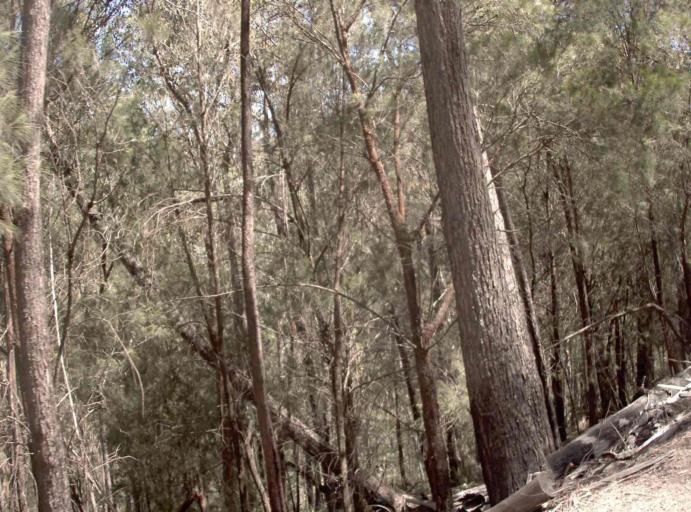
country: AU
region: Victoria
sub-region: East Gippsland
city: Lakes Entrance
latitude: -37.3750
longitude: 148.2176
